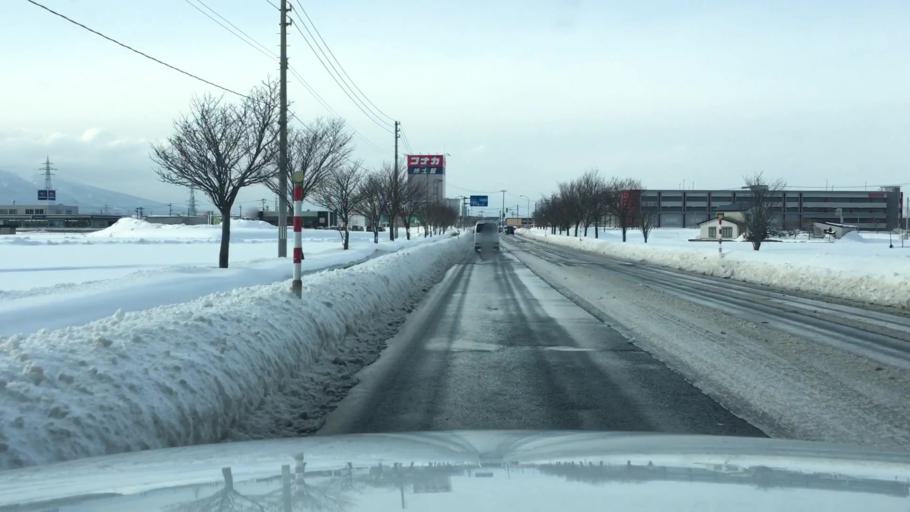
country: JP
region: Aomori
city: Hirosaki
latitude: 40.5971
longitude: 140.5158
